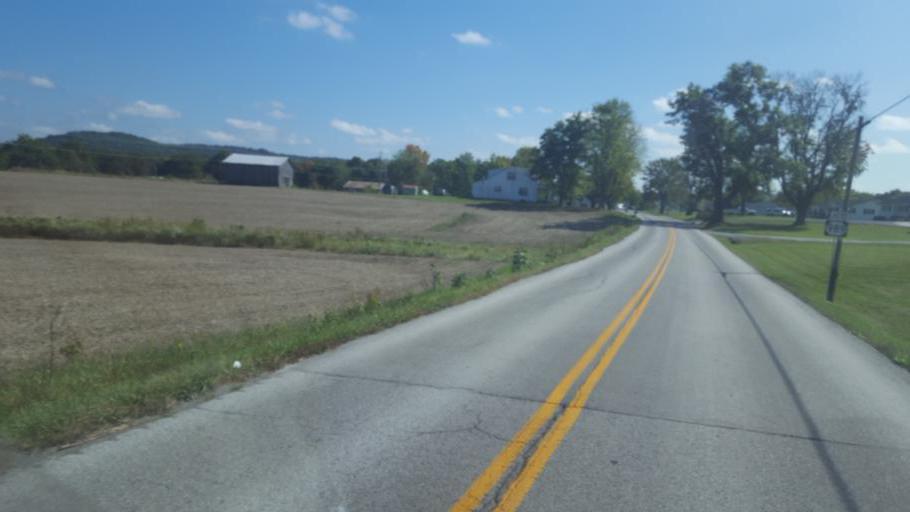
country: US
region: Kentucky
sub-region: Fleming County
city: Flemingsburg
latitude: 38.4790
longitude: -83.6060
